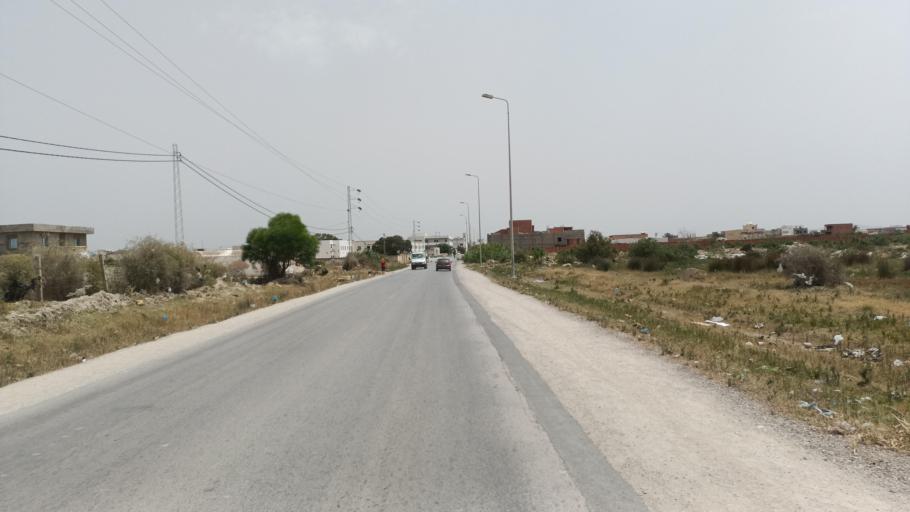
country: TN
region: Nabul
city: Manzil Bu Zalafah
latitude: 36.7095
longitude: 10.4833
